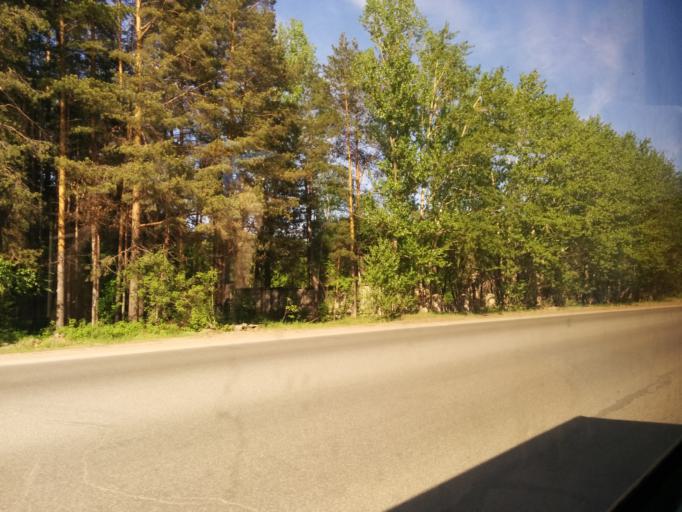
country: RU
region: Perm
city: Kondratovo
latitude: 58.0395
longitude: 56.1313
